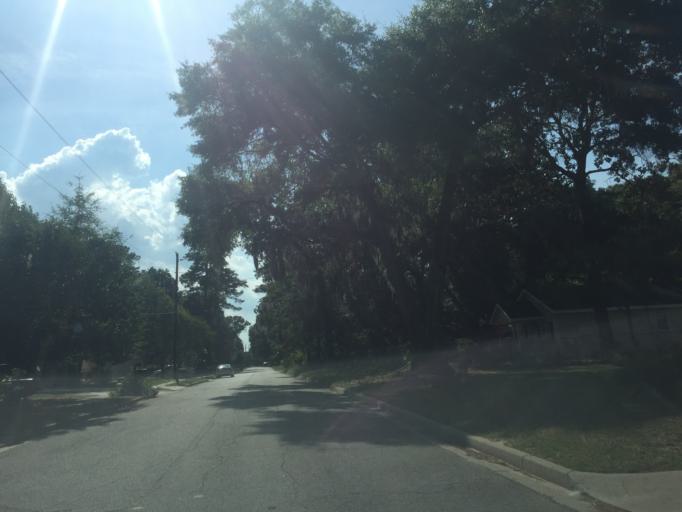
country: US
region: Georgia
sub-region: Chatham County
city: Isle of Hope
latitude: 31.9847
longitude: -81.1001
